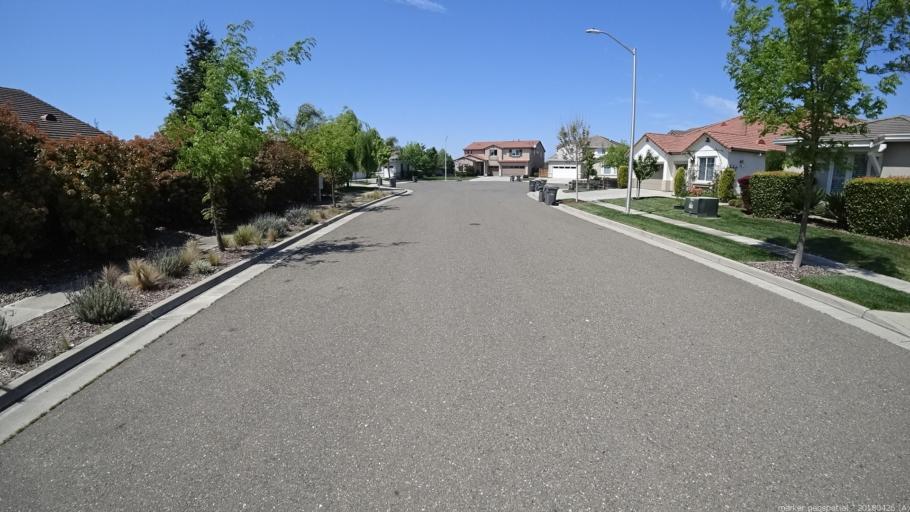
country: US
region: California
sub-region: Yolo County
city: West Sacramento
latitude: 38.5300
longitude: -121.5772
